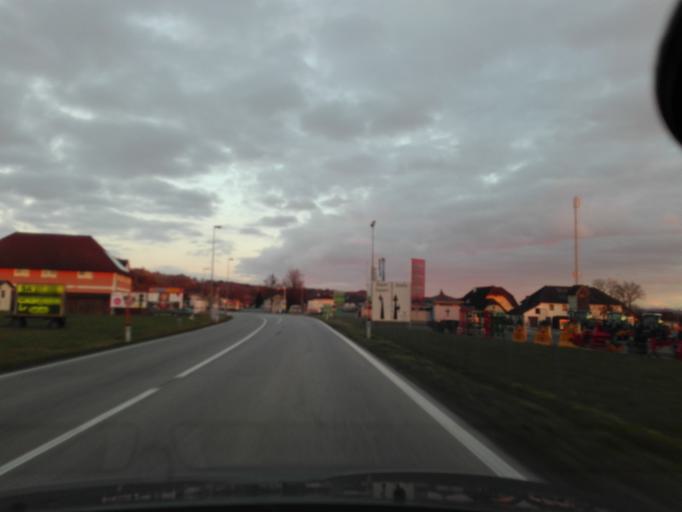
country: AT
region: Upper Austria
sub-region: Politischer Bezirk Perg
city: Bad Kreuzen
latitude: 48.2069
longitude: 14.7876
